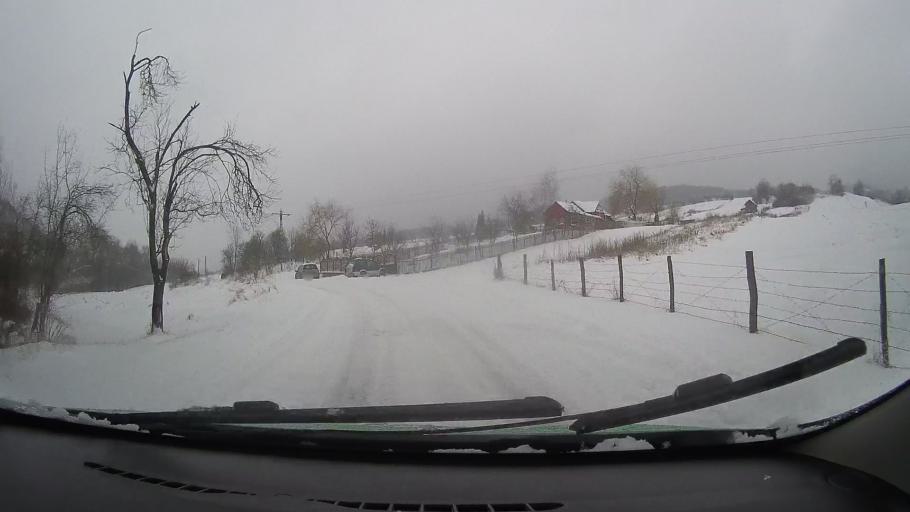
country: RO
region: Hunedoara
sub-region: Comuna Carjiti
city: Carjiti
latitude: 45.8424
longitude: 22.8335
